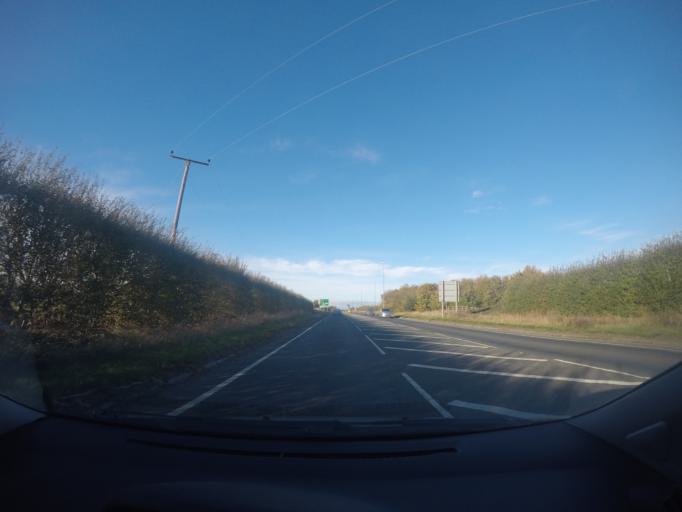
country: GB
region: England
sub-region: City of York
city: Copmanthorpe
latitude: 53.9333
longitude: -1.1444
